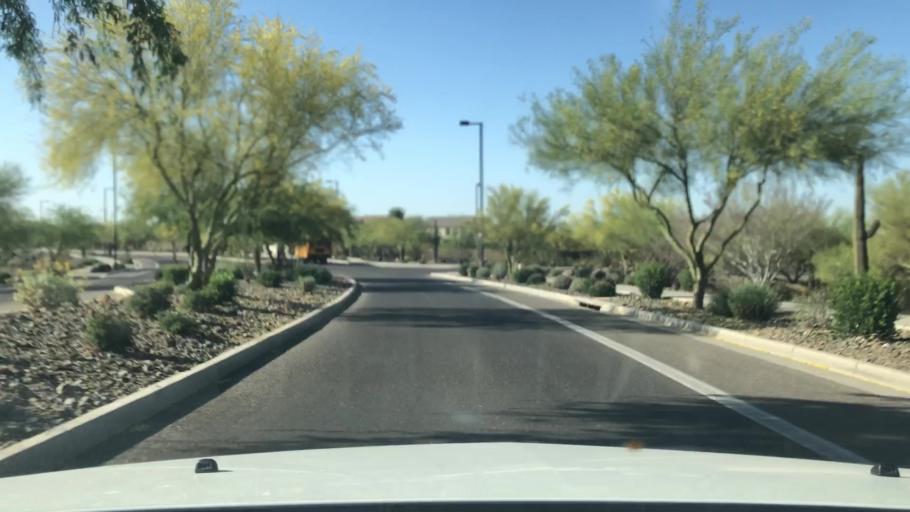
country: US
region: Arizona
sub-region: Maricopa County
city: Anthem
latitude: 33.7320
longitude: -112.0941
